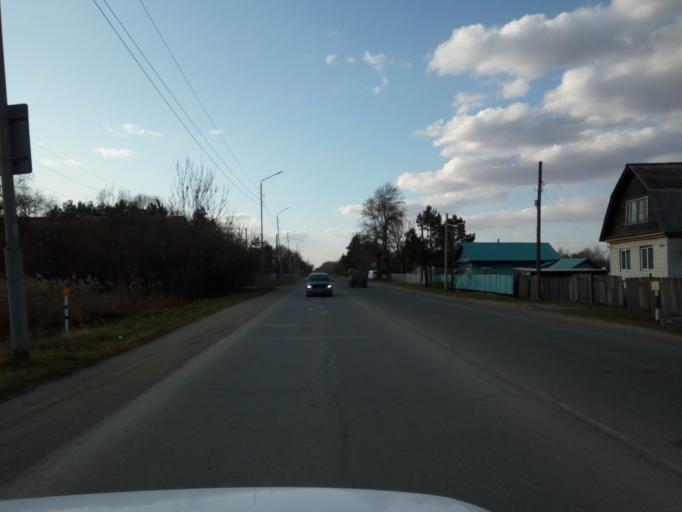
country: RU
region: Primorskiy
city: Dal'nerechensk
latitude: 45.9188
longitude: 133.7591
